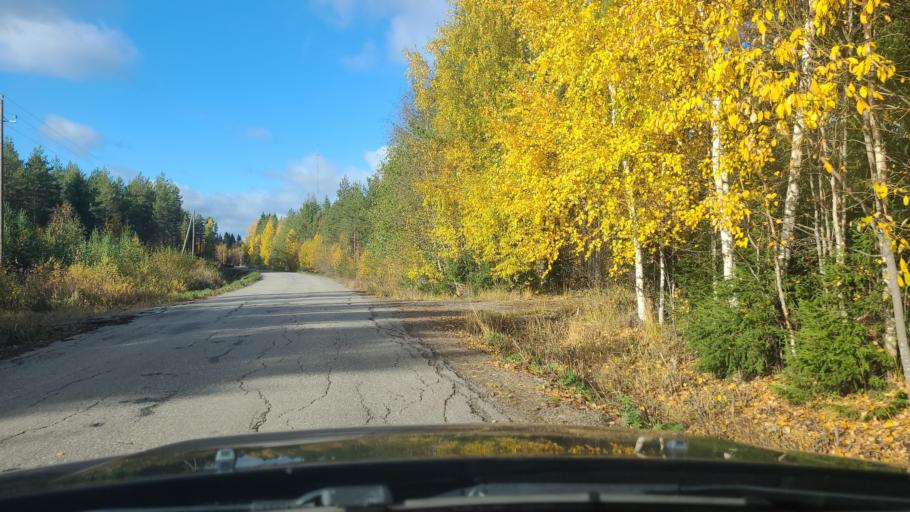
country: FI
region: Southern Savonia
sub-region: Pieksaemaeki
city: Juva
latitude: 61.8039
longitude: 27.5924
